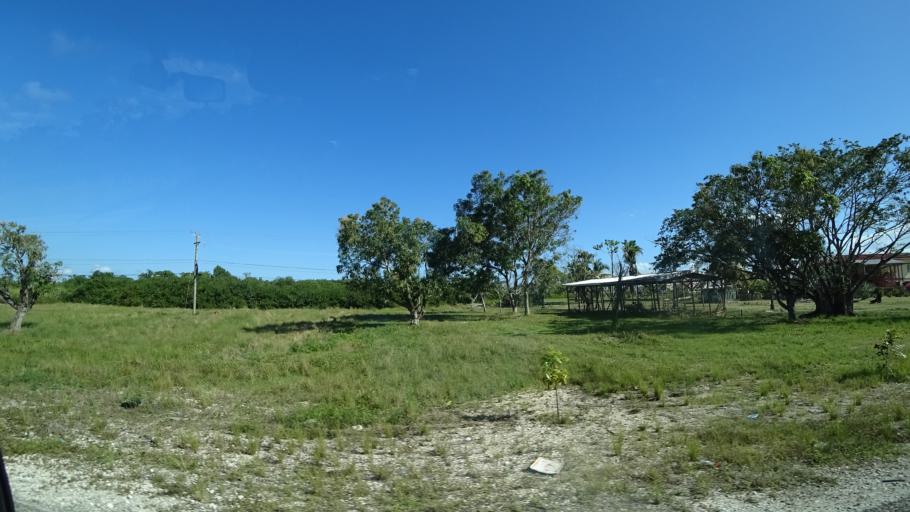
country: BZ
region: Belize
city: Belize City
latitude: 17.5434
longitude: -88.2660
